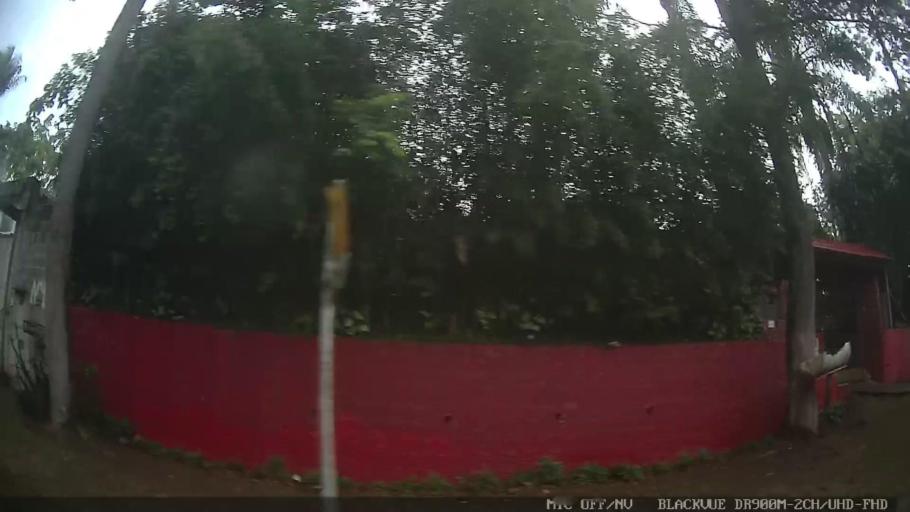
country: BR
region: Sao Paulo
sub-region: Ribeirao Pires
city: Ribeirao Pires
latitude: -23.7030
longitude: -46.3656
